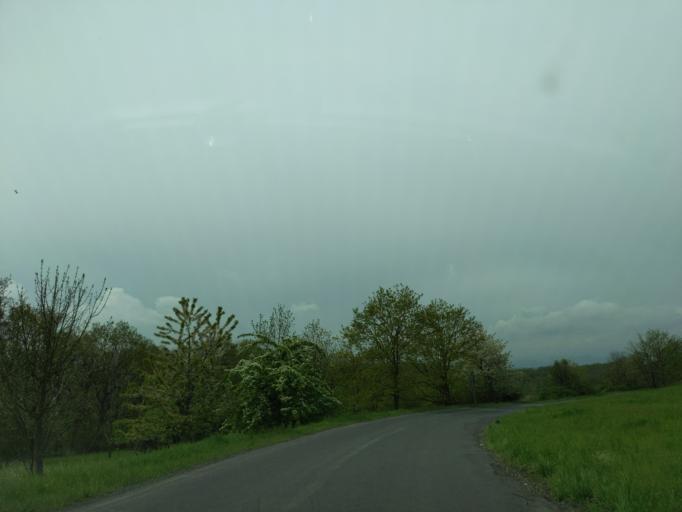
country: CZ
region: Ustecky
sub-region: Okres Usti nad Labem
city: Usti nad Labem
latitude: 50.6937
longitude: 14.0681
